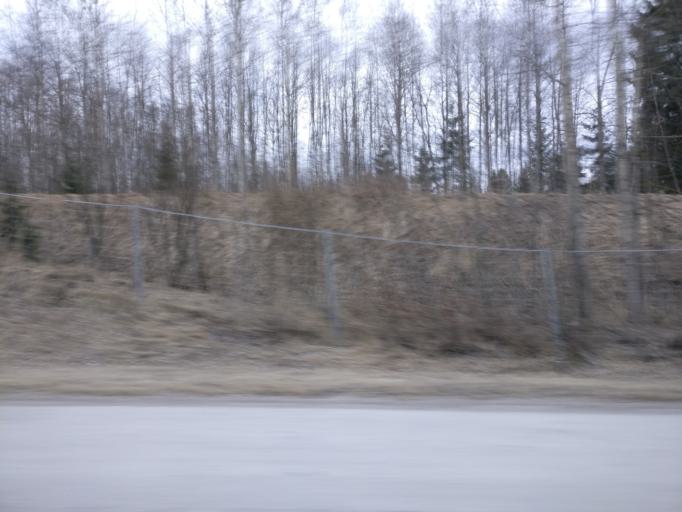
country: FI
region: Uusimaa
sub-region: Helsinki
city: Hyvinge
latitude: 60.5925
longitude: 24.7973
